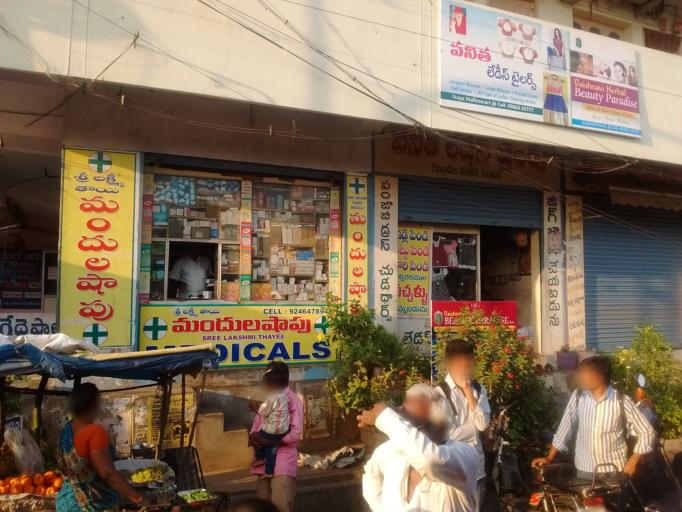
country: IN
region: Andhra Pradesh
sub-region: Krishna
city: Vijayawada
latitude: 16.5233
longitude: 80.6665
